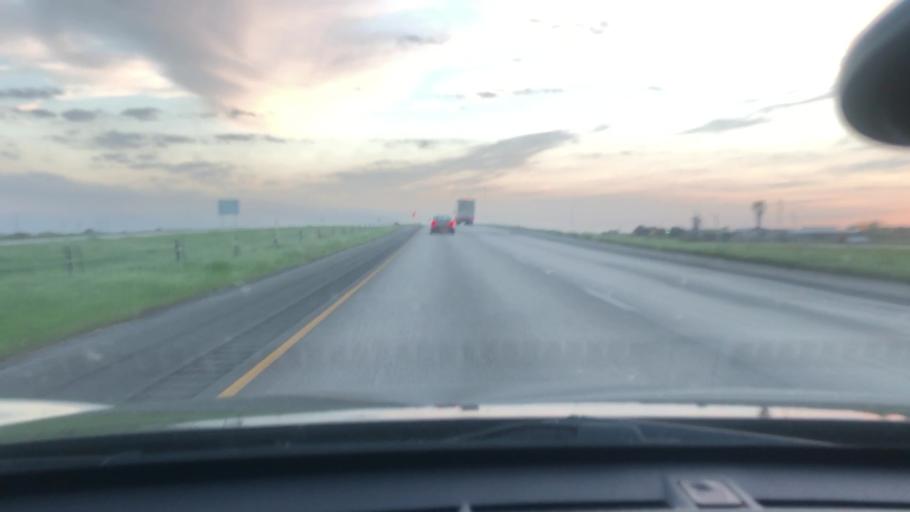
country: US
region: Texas
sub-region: Jackson County
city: Edna
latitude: 28.9713
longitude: -96.6695
